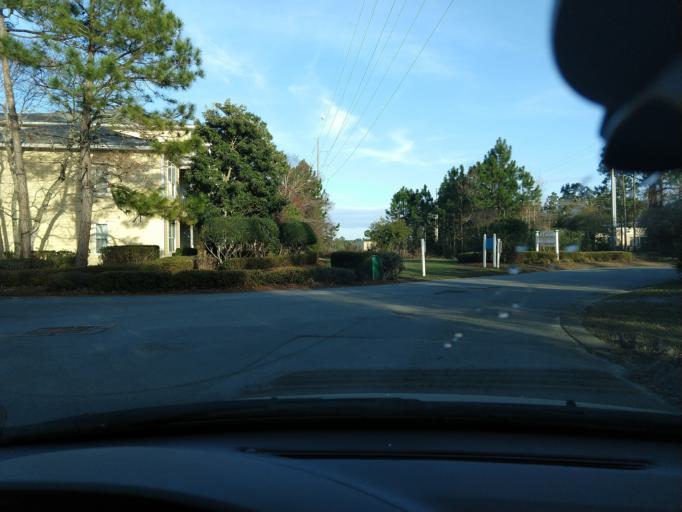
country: US
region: Florida
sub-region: Walton County
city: Miramar Beach
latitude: 30.3803
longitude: -86.3102
